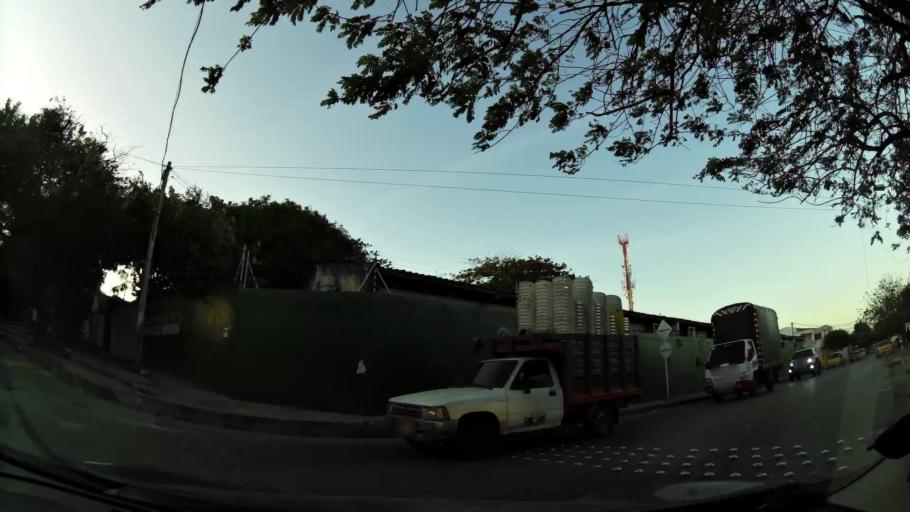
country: CO
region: Atlantico
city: Barranquilla
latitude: 10.9743
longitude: -74.8081
